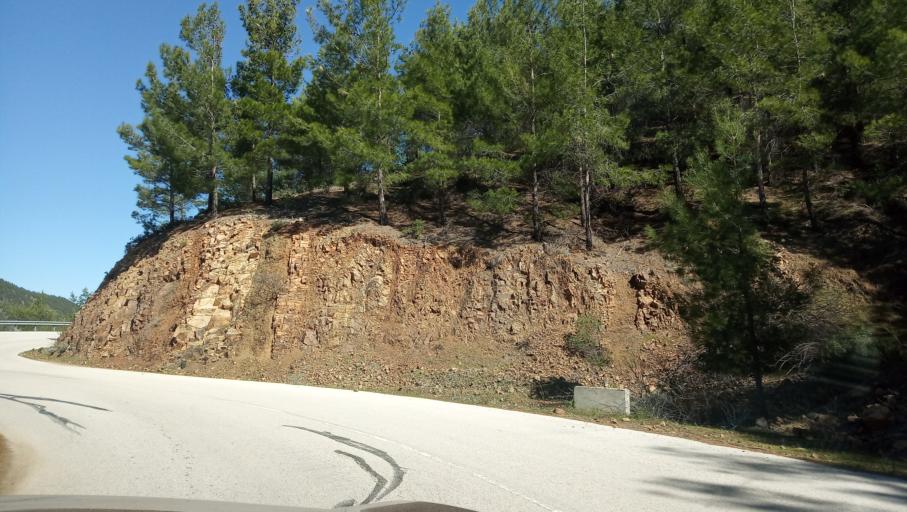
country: CY
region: Lefkosia
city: Lefka
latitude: 35.0689
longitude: 32.7507
